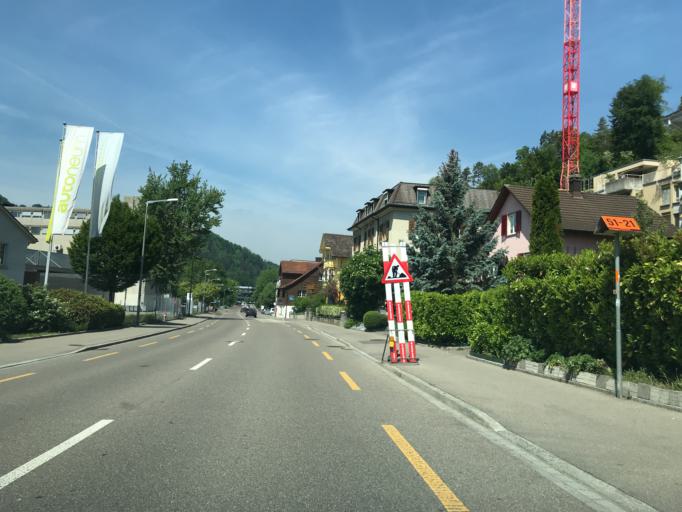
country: CH
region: Zurich
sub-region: Bezirk Winterthur
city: Toess (Kreis 4) / Schlosstal
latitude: 47.4962
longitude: 8.7033
